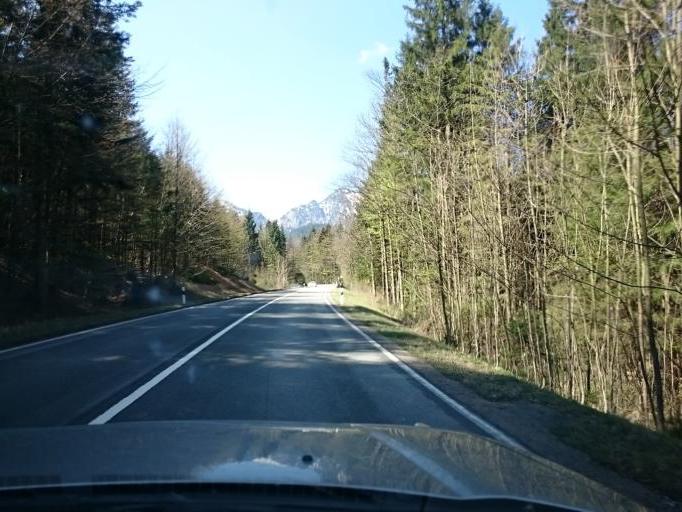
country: DE
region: Bavaria
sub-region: Upper Bavaria
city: Kochel
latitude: 47.6264
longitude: 11.3534
